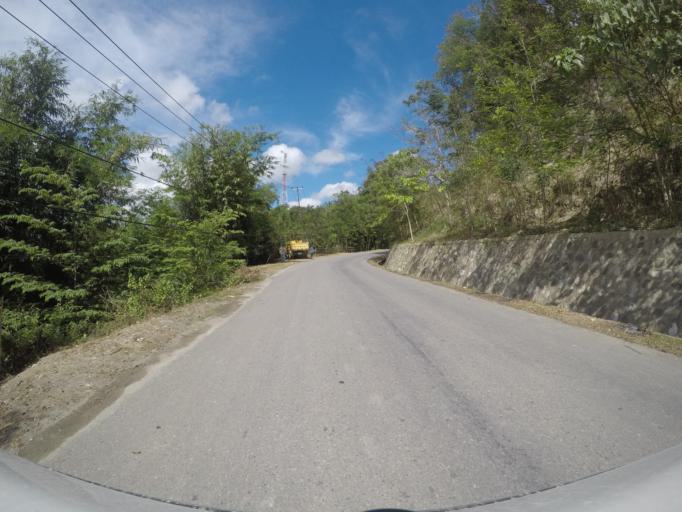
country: TL
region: Viqueque
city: Viqueque
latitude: -8.8688
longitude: 126.3629
